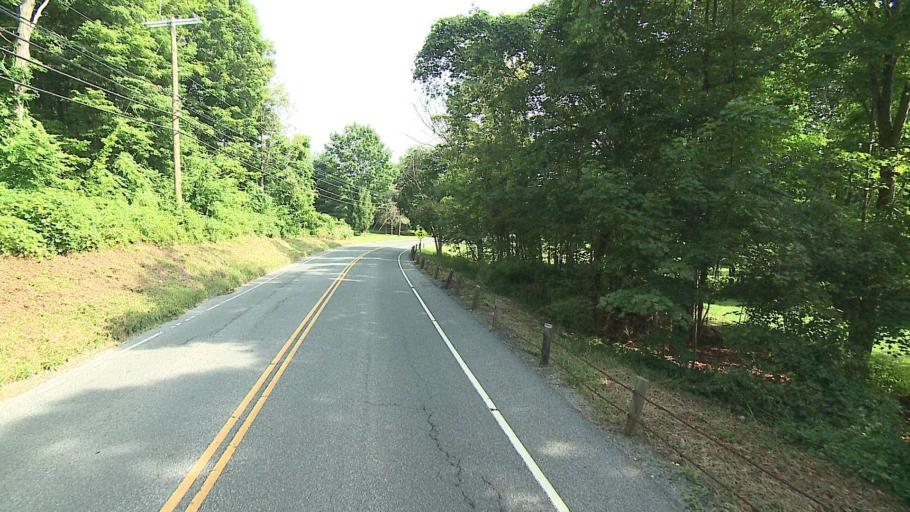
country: US
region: Connecticut
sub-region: Fairfield County
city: Sherman
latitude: 41.5916
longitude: -73.4726
